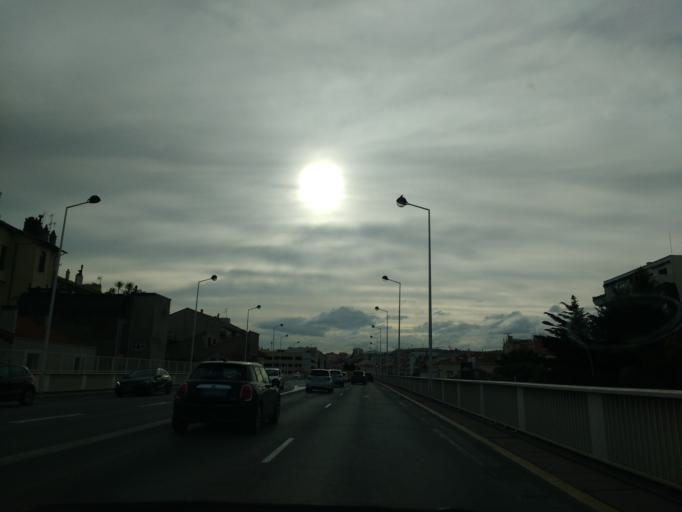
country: FR
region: Provence-Alpes-Cote d'Azur
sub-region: Departement des Alpes-Maritimes
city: Cannes
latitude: 43.5540
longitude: 7.0245
